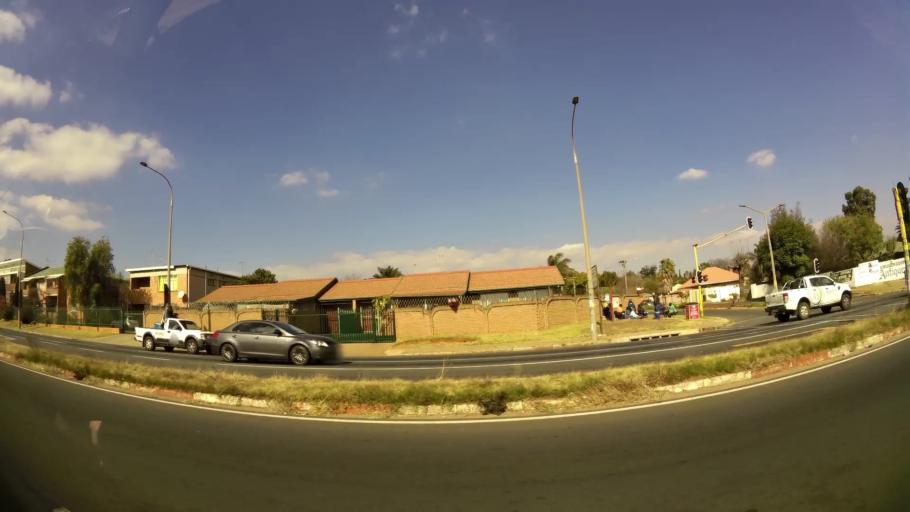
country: ZA
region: Gauteng
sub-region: West Rand District Municipality
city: Krugersdorp
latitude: -26.0891
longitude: 27.7827
